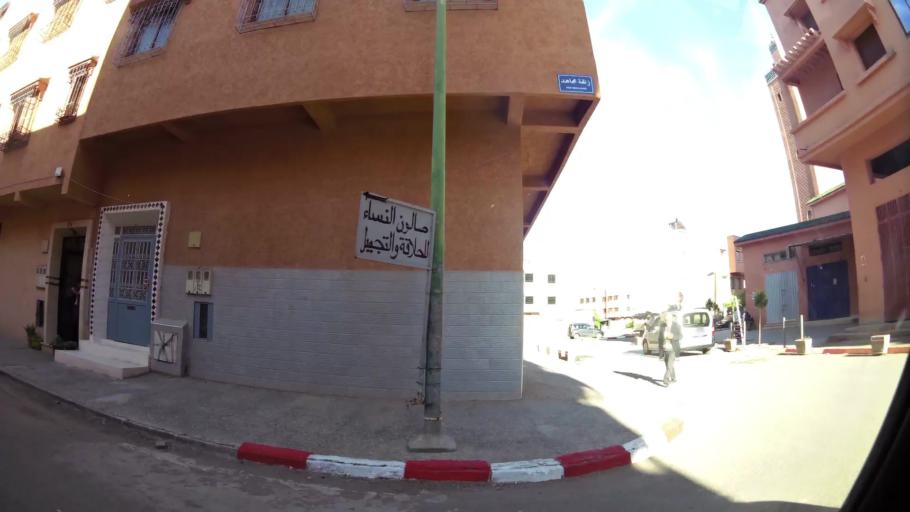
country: MA
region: Marrakech-Tensift-Al Haouz
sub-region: Marrakech
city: Marrakesh
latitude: 31.6226
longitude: -8.0695
